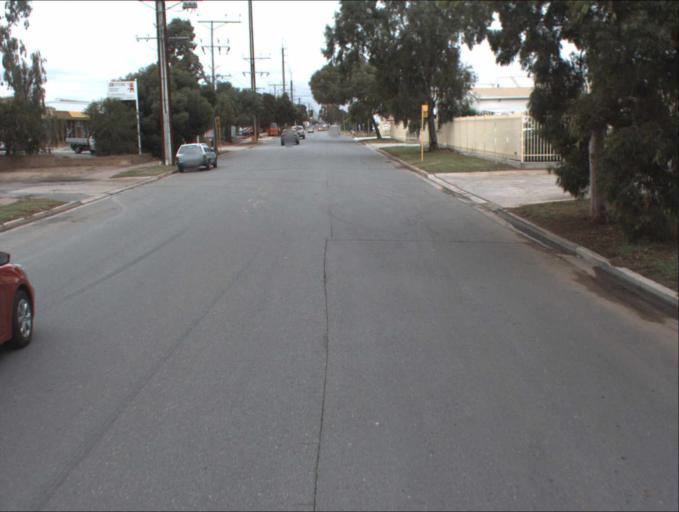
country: AU
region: South Australia
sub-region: Port Adelaide Enfield
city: Blair Athol
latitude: -34.8436
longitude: 138.5820
